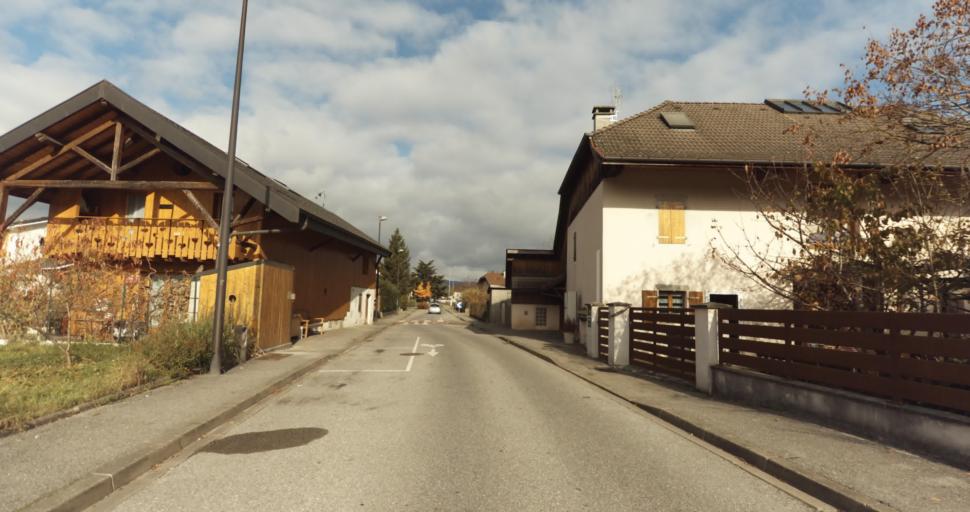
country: FR
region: Rhone-Alpes
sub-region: Departement de la Haute-Savoie
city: Meythet
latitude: 45.9198
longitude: 6.0983
